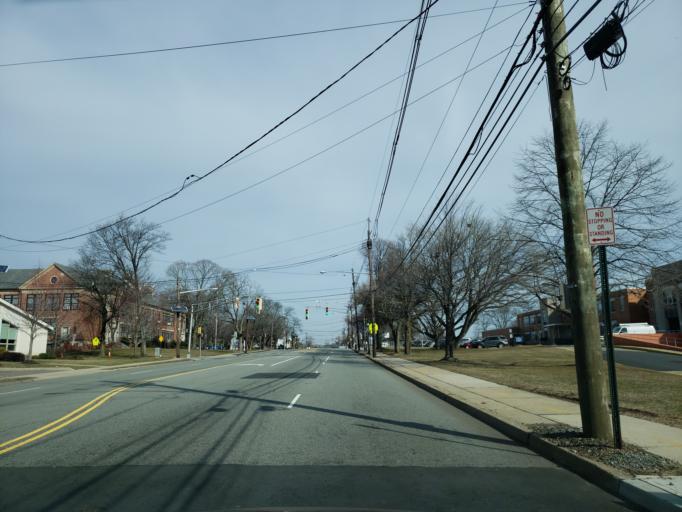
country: US
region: New Jersey
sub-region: Essex County
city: West Orange
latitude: 40.8063
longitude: -74.2621
